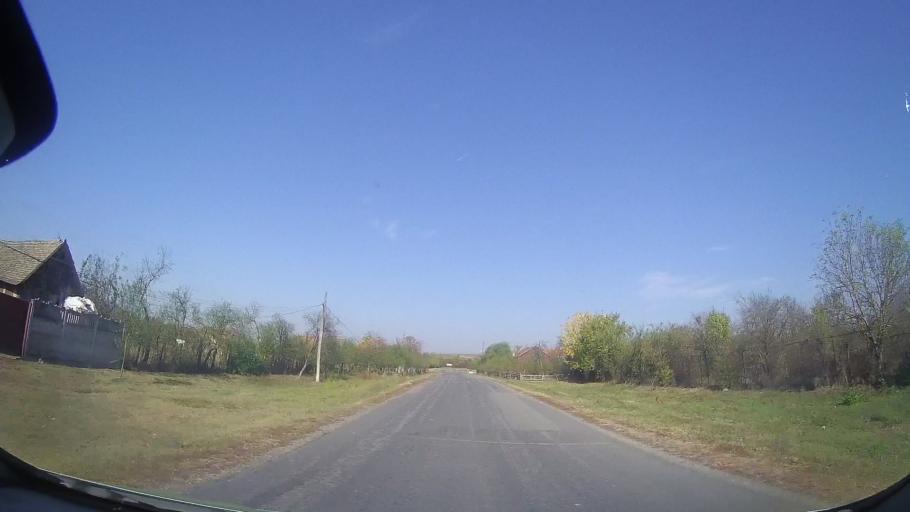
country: RO
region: Timis
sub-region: Comuna Ghizela
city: Ghizela
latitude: 45.8205
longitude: 21.7416
